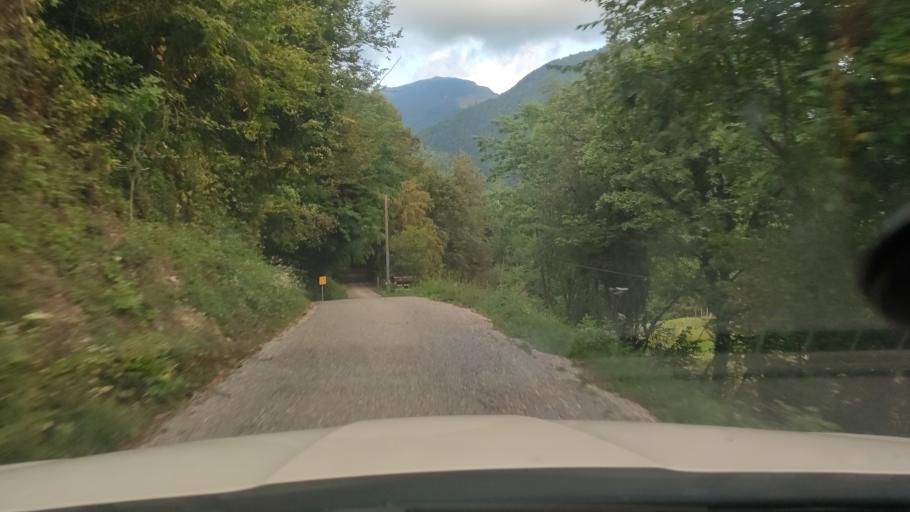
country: IT
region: Friuli Venezia Giulia
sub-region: Provincia di Udine
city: Cras
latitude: 46.2158
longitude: 13.6479
